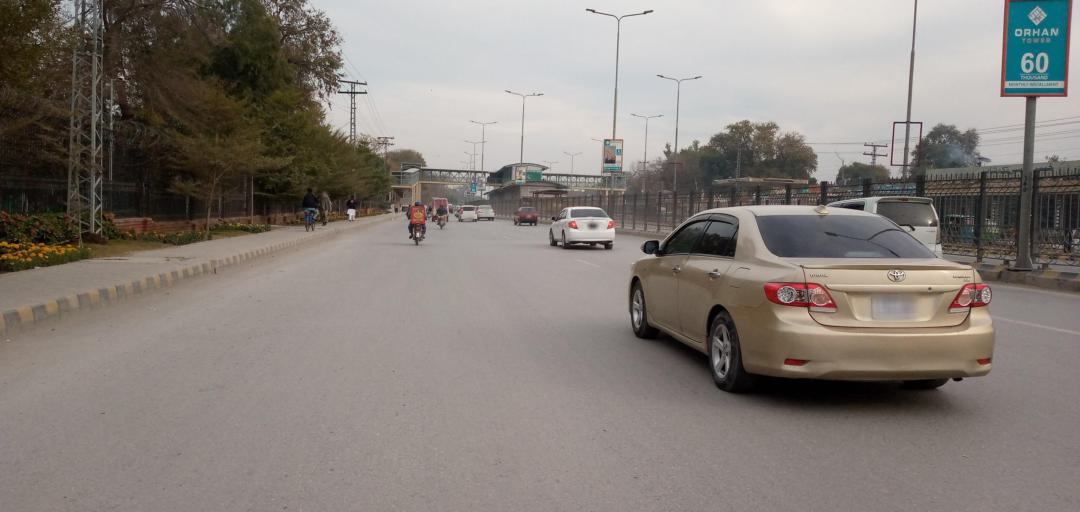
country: PK
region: Khyber Pakhtunkhwa
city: Peshawar
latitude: 33.9985
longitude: 71.4763
